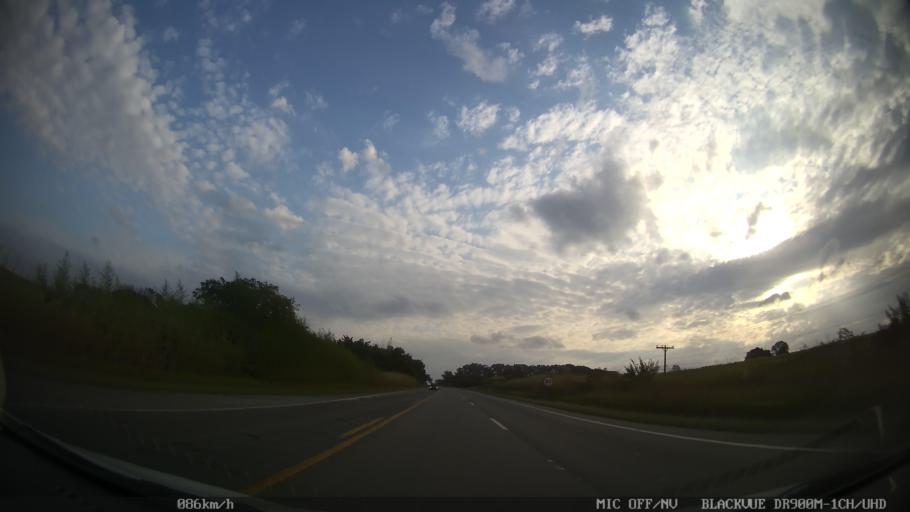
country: BR
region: Sao Paulo
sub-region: Cosmopolis
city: Cosmopolis
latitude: -22.6320
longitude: -47.2995
